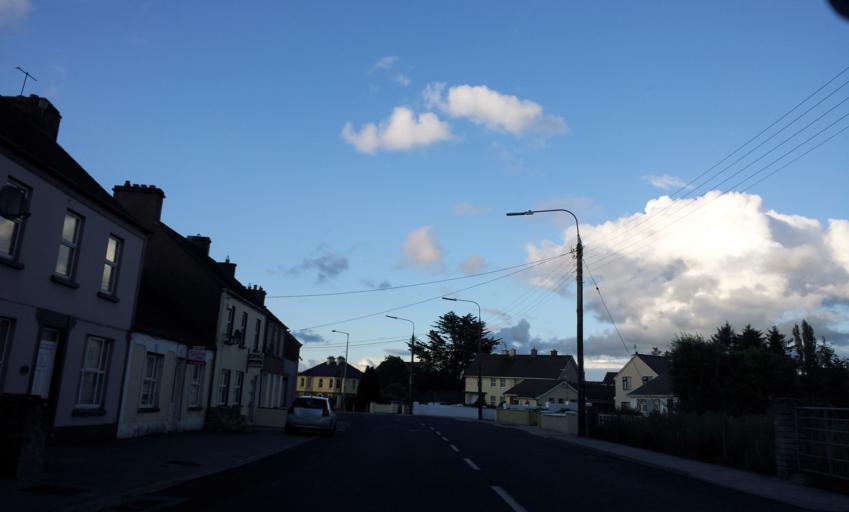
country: IE
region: Munster
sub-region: County Limerick
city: Abbeyfeale
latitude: 52.3807
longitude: -9.3025
